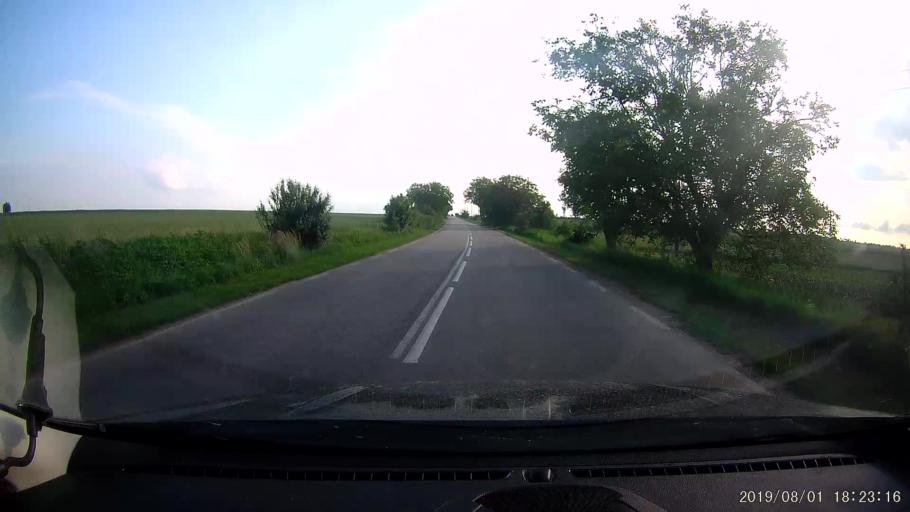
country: BG
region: Shumen
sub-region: Obshtina Kaolinovo
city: Kaolinovo
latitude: 43.6318
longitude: 27.0290
